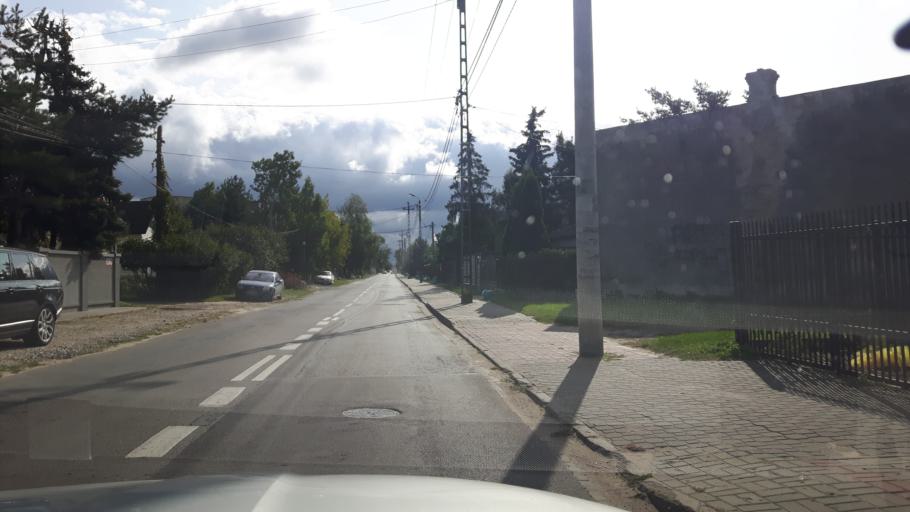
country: PL
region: Masovian Voivodeship
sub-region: Powiat wolominski
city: Marki
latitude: 52.3276
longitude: 21.0962
